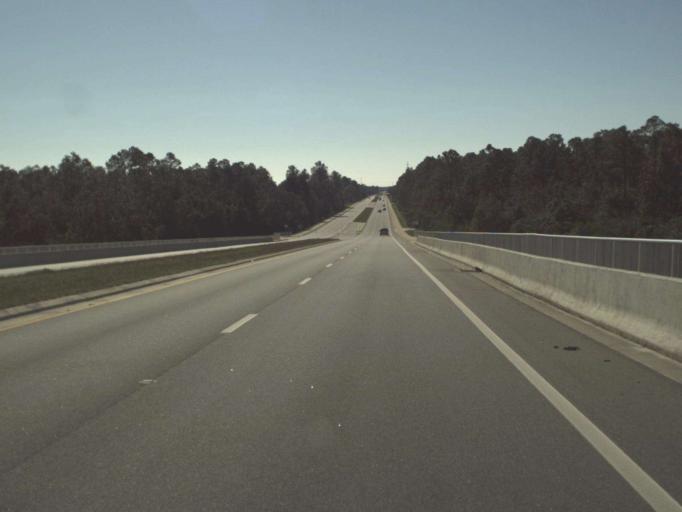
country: US
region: Florida
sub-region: Santa Rosa County
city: Bagdad
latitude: 30.5684
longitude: -87.0871
